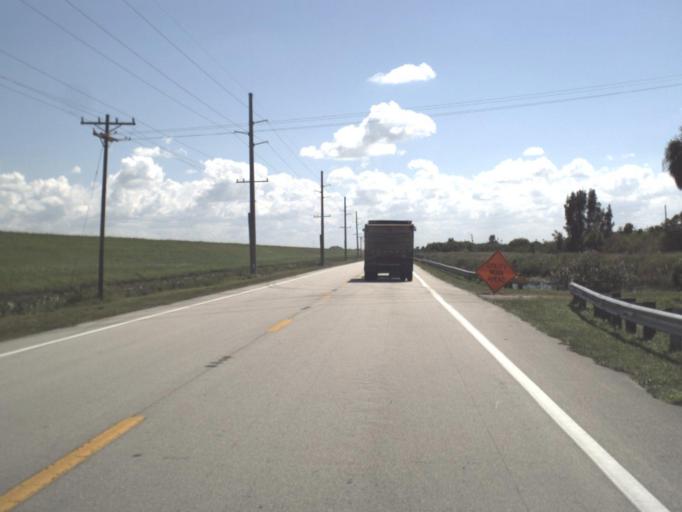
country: US
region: Florida
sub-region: Glades County
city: Moore Haven
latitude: 26.9007
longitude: -81.1225
